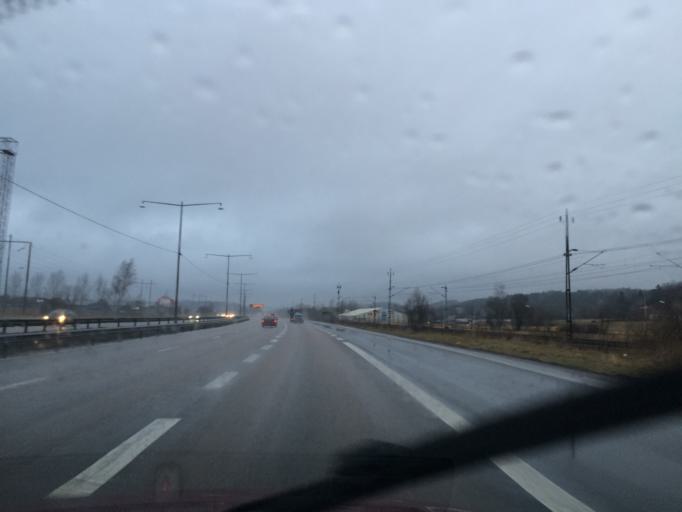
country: SE
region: Vaestra Goetaland
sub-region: Molndal
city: Kallered
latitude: 57.6332
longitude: 12.0341
